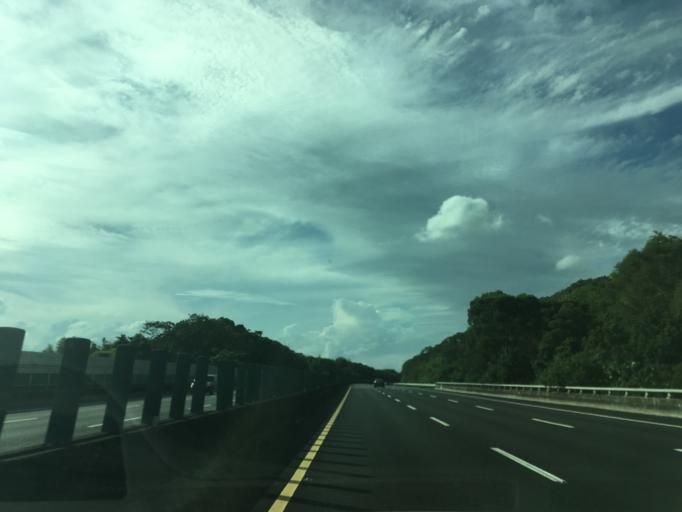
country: TW
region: Taiwan
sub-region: Nantou
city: Nantou
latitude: 23.8373
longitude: 120.7068
